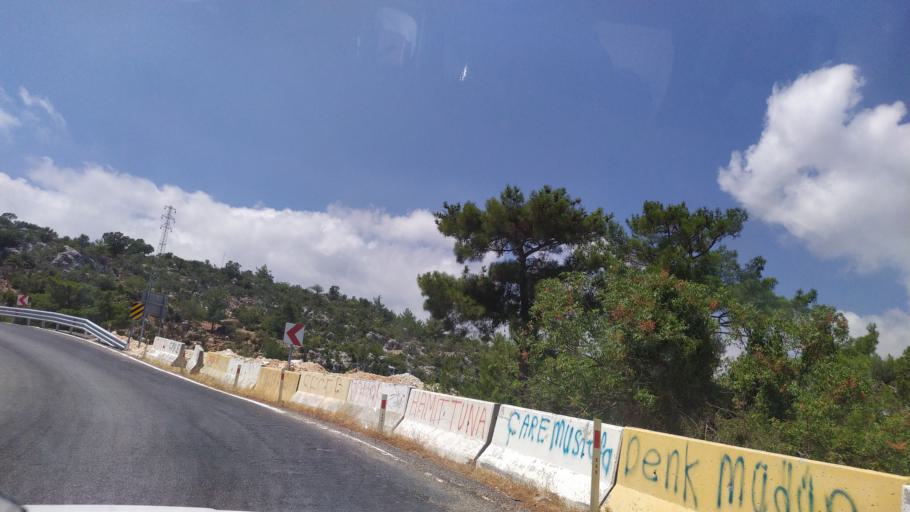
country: TR
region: Mersin
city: Gulnar
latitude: 36.2755
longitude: 33.3783
